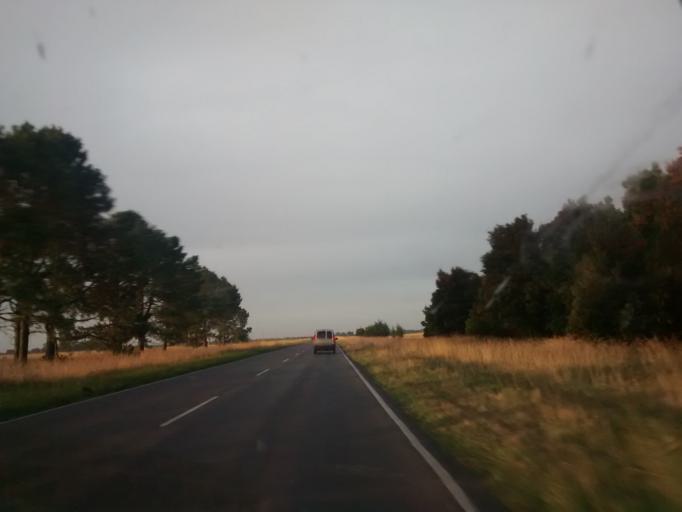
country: AR
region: Buenos Aires
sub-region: Partido de General Belgrano
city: General Belgrano
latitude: -35.9171
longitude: -58.6194
